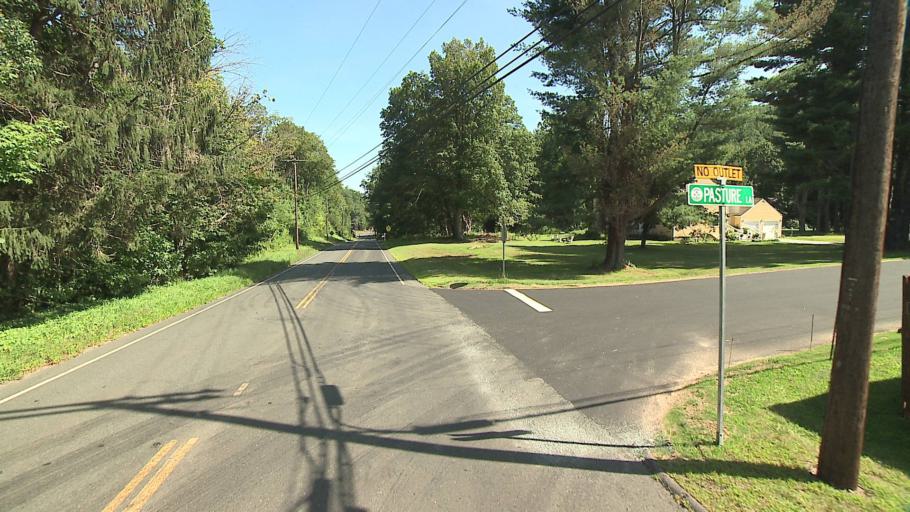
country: US
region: Connecticut
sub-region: Hartford County
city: West Simsbury
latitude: 41.8787
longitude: -72.8659
